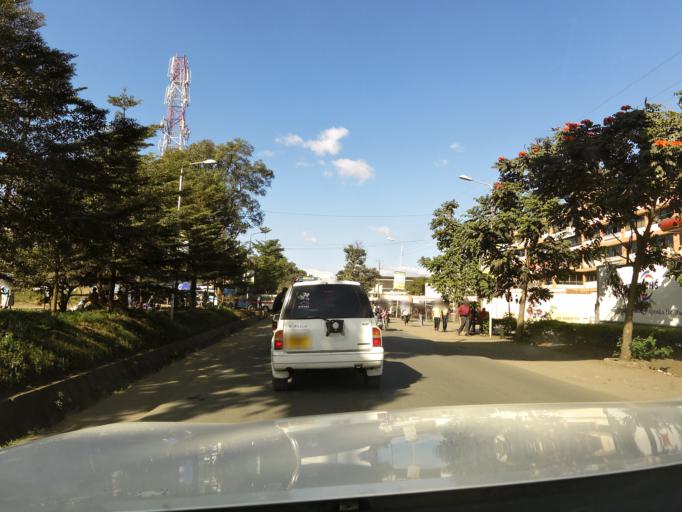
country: TZ
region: Arusha
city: Arusha
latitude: -3.3748
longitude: 36.6799
